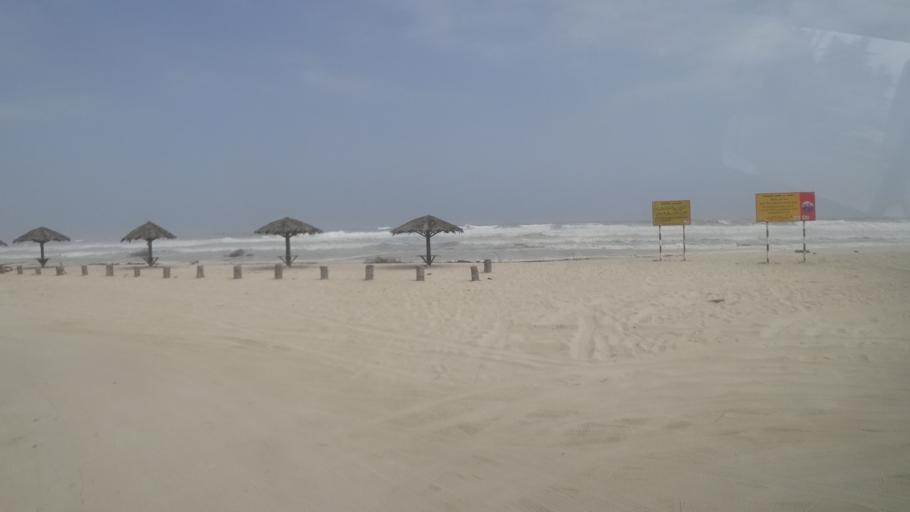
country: OM
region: Zufar
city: Salalah
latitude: 17.0087
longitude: 54.1574
